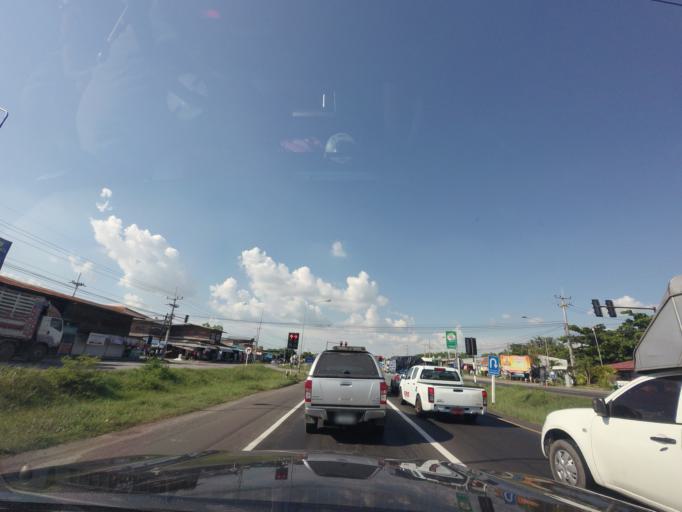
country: TH
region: Nakhon Ratchasima
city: Bua Lai
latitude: 15.6387
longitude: 102.5693
